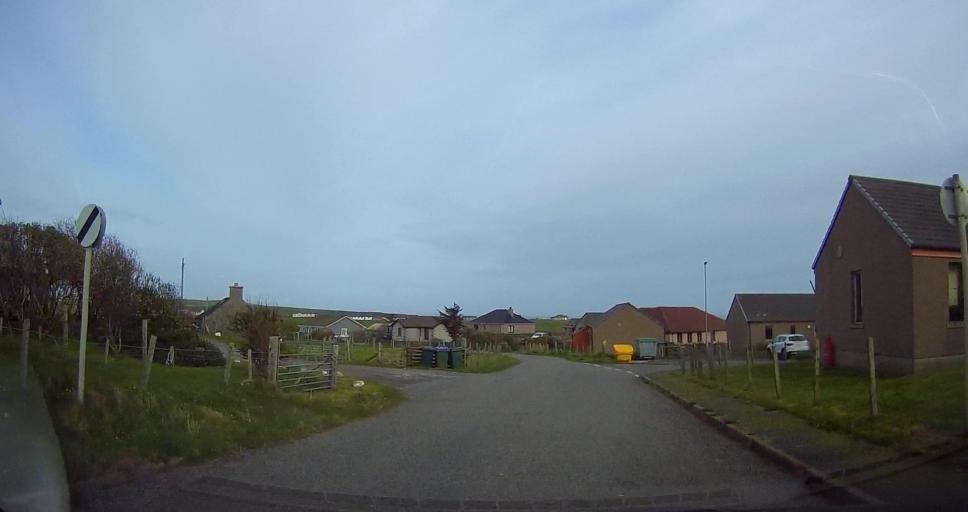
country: GB
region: Scotland
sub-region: Shetland Islands
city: Sandwick
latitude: 60.0387
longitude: -1.2292
